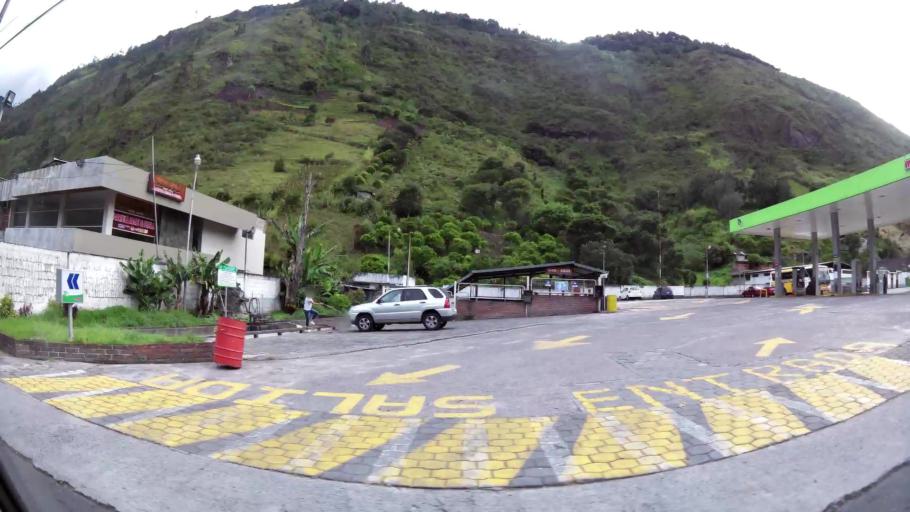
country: EC
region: Tungurahua
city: Banos
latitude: -1.3943
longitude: -78.4114
